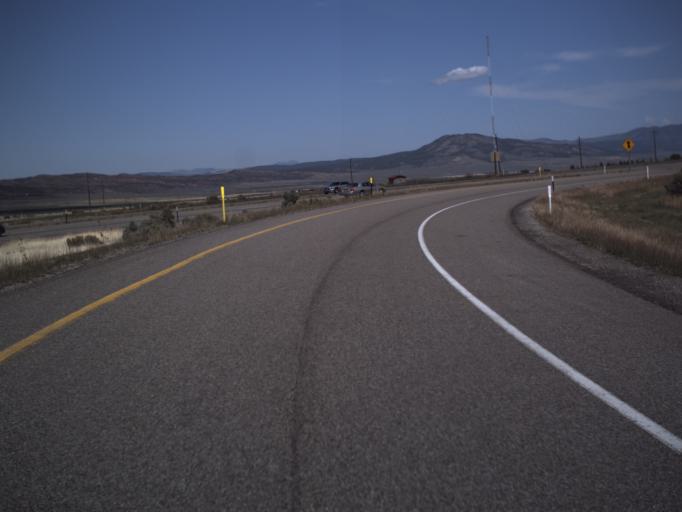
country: US
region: Utah
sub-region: Iron County
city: Enoch
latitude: 37.8026
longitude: -112.9446
